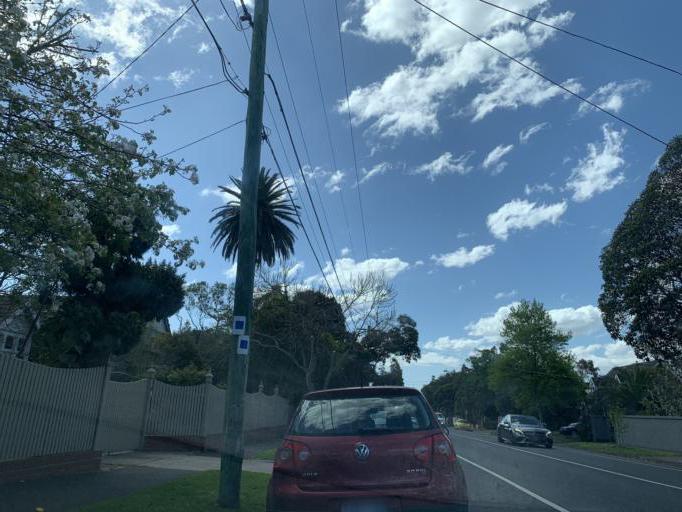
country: AU
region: Victoria
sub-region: Bayside
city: North Brighton
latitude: -37.9189
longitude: 144.9929
